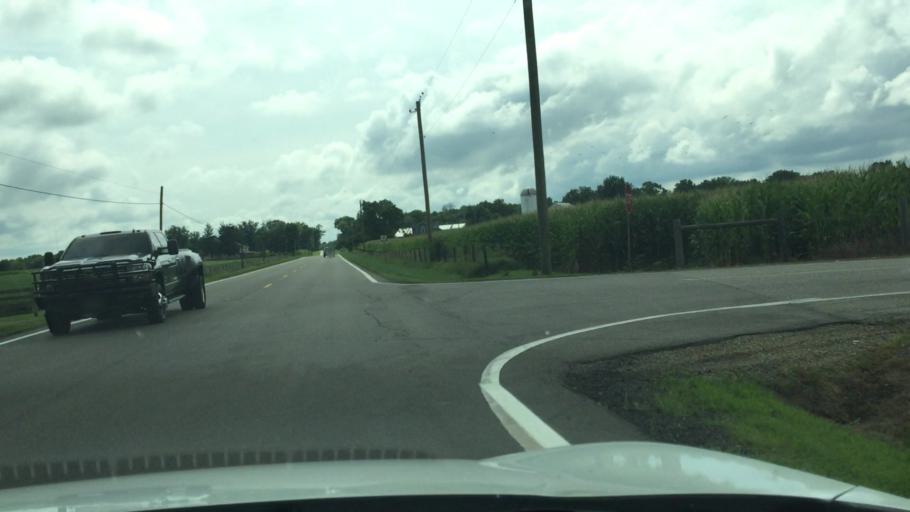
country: US
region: Ohio
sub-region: Clark County
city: Northridge
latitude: 40.0160
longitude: -83.6827
